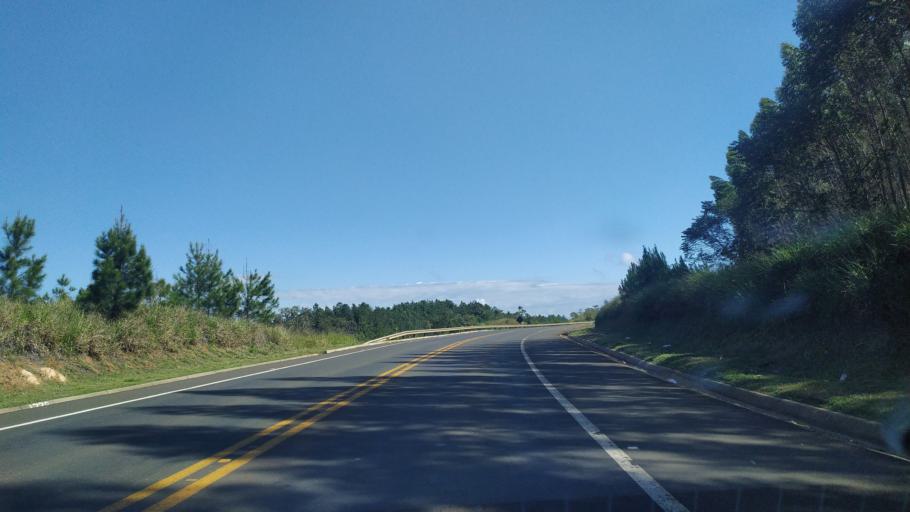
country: BR
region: Parana
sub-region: Ortigueira
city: Ortigueira
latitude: -24.2561
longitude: -50.7793
